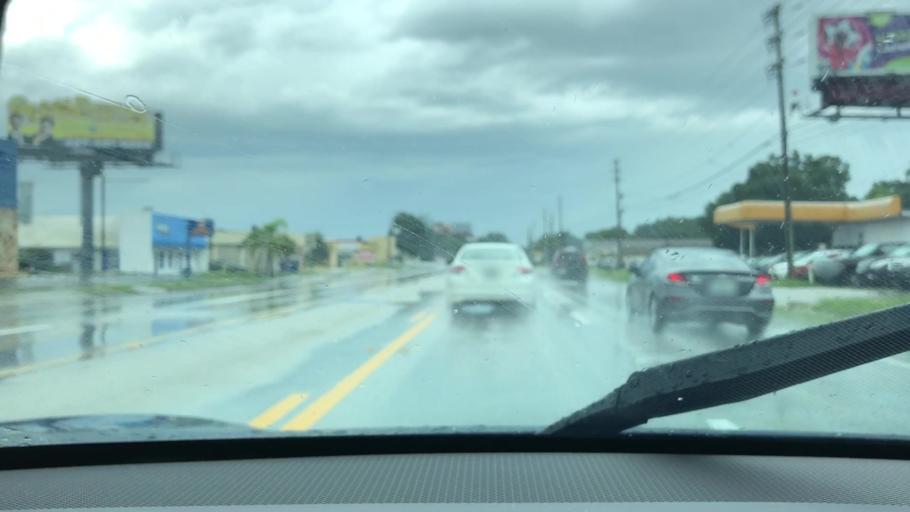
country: US
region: Florida
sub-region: Orange County
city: Pine Castle
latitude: 28.4663
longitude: -81.3676
